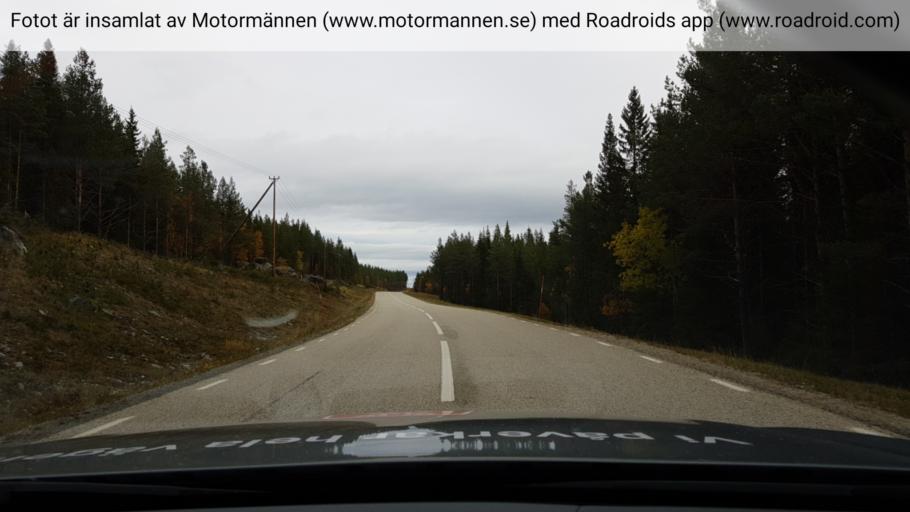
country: SE
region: Jaemtland
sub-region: Are Kommun
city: Are
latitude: 62.8101
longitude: 12.9588
